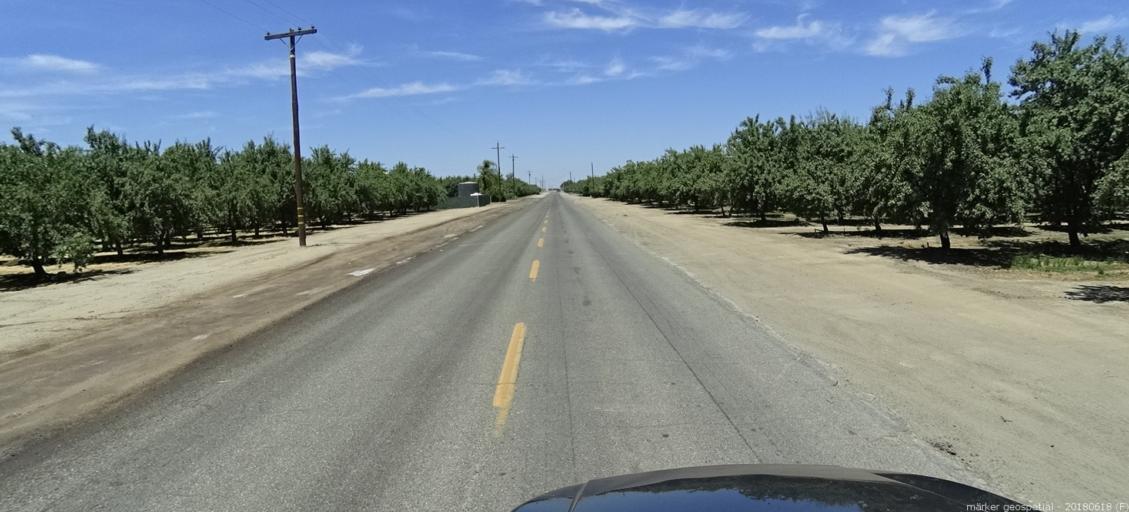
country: US
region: California
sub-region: Madera County
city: Parkwood
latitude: 36.9187
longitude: -120.0924
